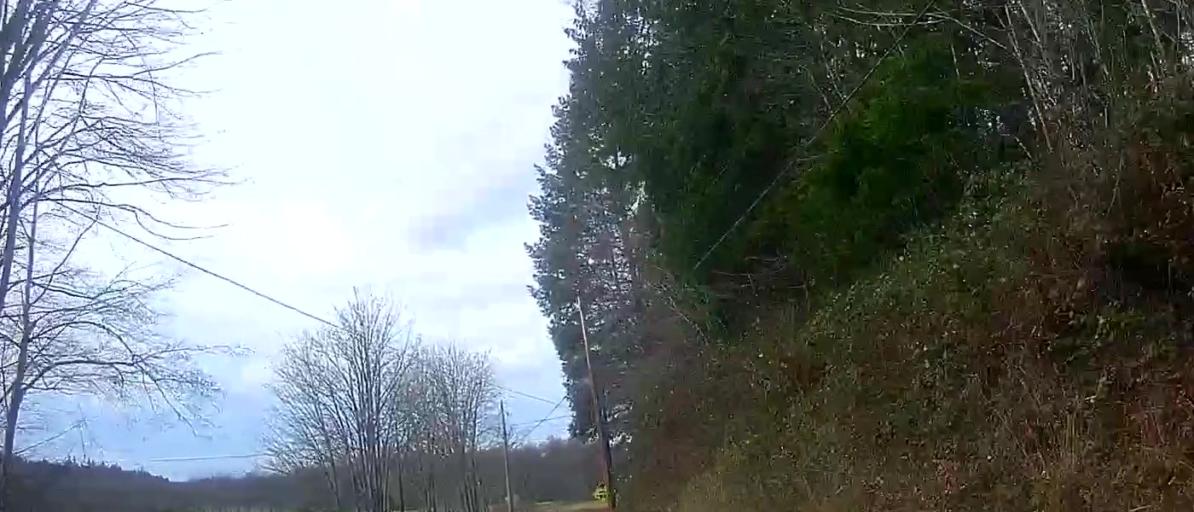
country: US
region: Washington
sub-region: Skagit County
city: Sedro-Woolley
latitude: 48.5547
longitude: -122.2945
